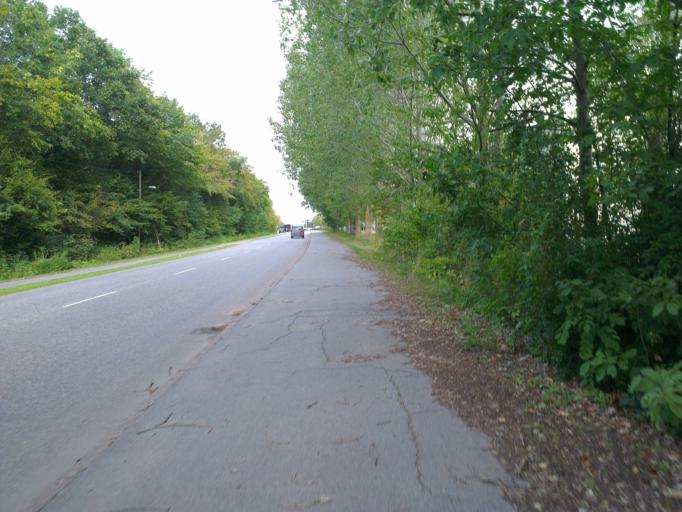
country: DK
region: Capital Region
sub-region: Frederikssund Kommune
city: Frederikssund
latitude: 55.8225
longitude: 12.0919
